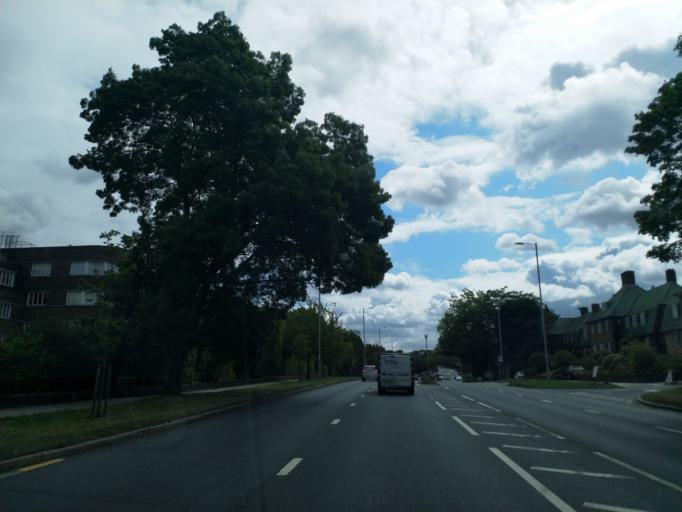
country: GB
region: England
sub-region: Greater London
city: Belsize Park
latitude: 51.5844
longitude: -0.1705
